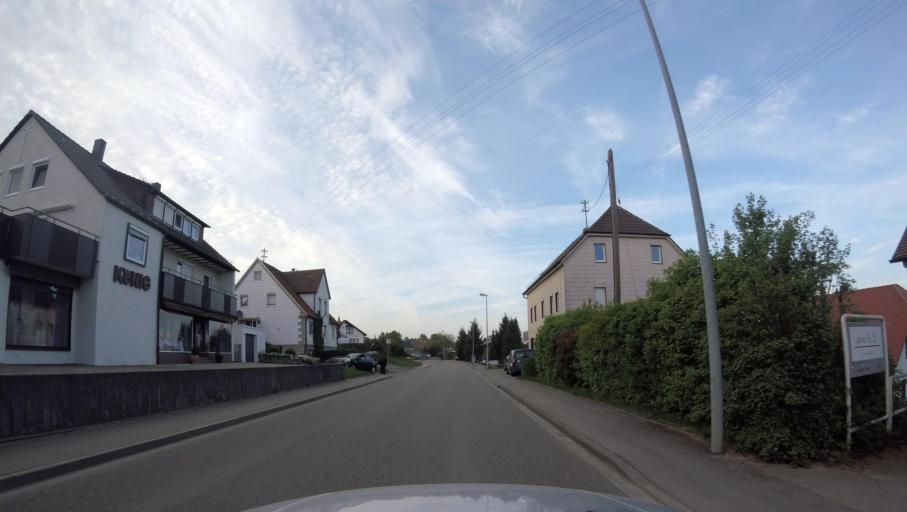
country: DE
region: Baden-Wuerttemberg
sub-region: Regierungsbezirk Stuttgart
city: Spraitbach
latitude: 48.8762
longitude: 9.7614
